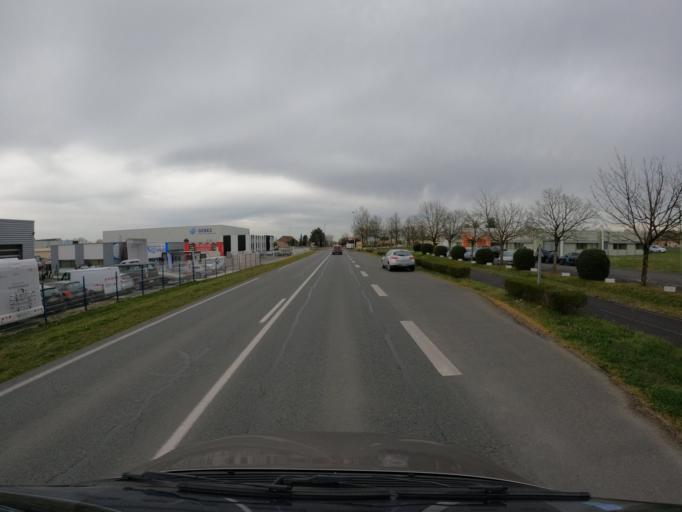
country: FR
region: Pays de la Loire
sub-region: Departement de la Vendee
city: Saint-Hilaire-de-Loulay
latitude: 46.9953
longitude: -1.3271
